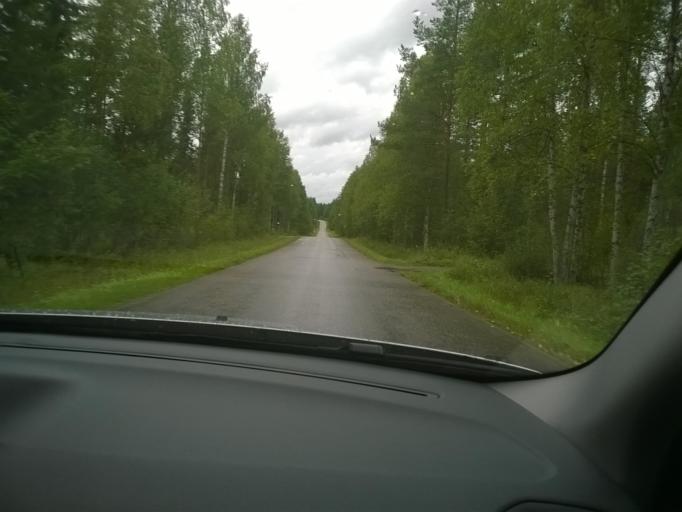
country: FI
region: Kainuu
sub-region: Kehys-Kainuu
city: Kuhmo
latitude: 64.1304
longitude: 29.4471
